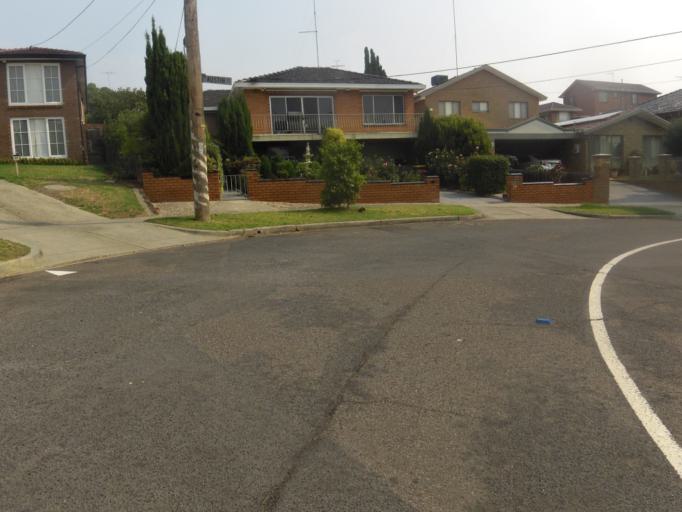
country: AU
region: Victoria
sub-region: Manningham
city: Bulleen
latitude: -37.7661
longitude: 145.0871
